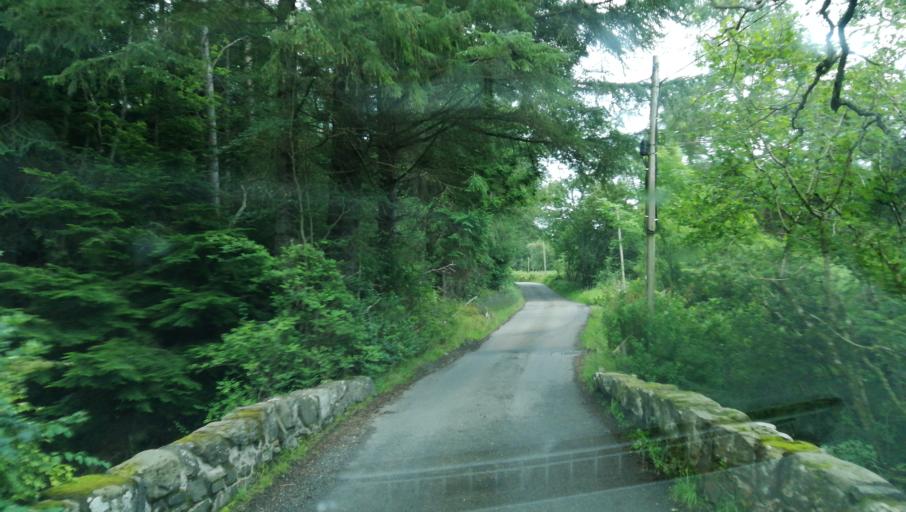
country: GB
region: Scotland
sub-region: Perth and Kinross
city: Blairgowrie
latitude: 56.6931
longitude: -3.4035
